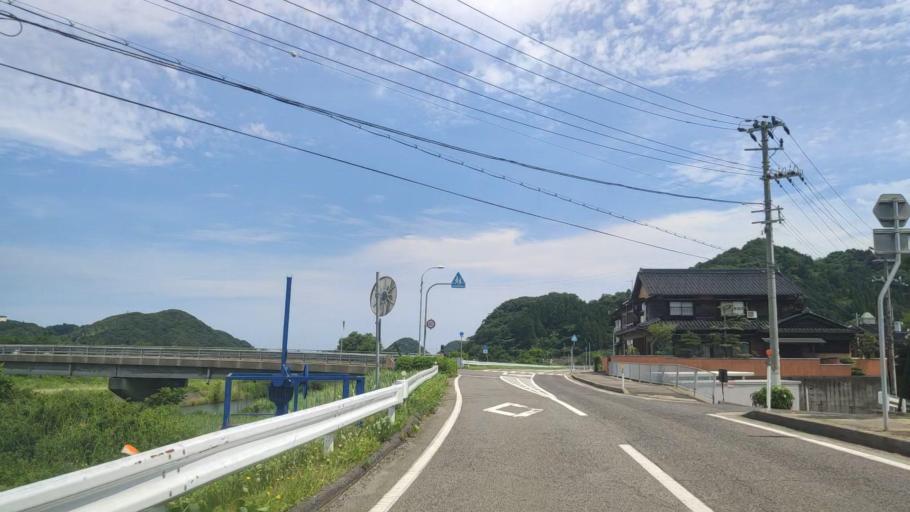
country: JP
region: Hyogo
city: Toyooka
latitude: 35.6479
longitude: 134.7637
